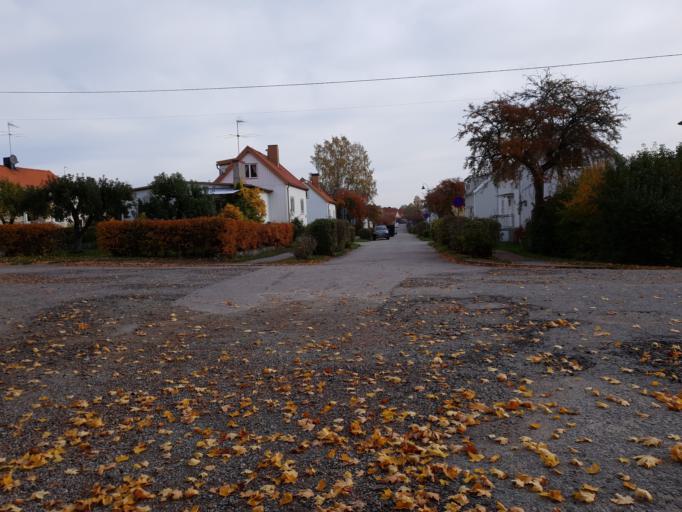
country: SE
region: Stockholm
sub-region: Stockholms Kommun
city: Bromma
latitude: 59.3474
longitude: 17.9015
